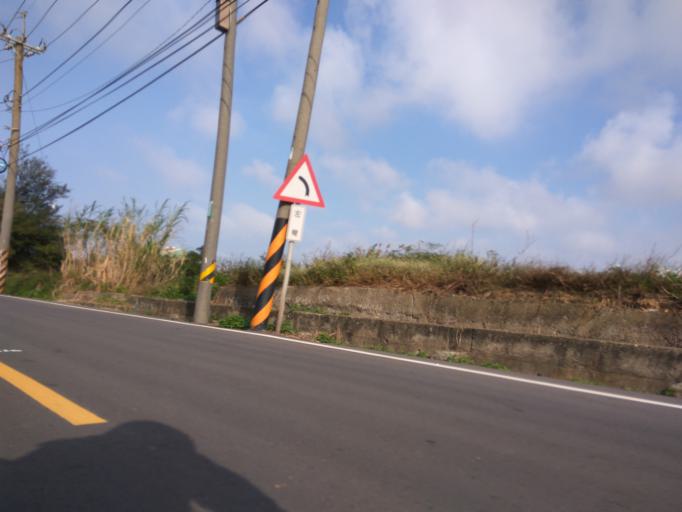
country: TW
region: Taiwan
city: Taoyuan City
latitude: 25.0684
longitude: 121.1730
